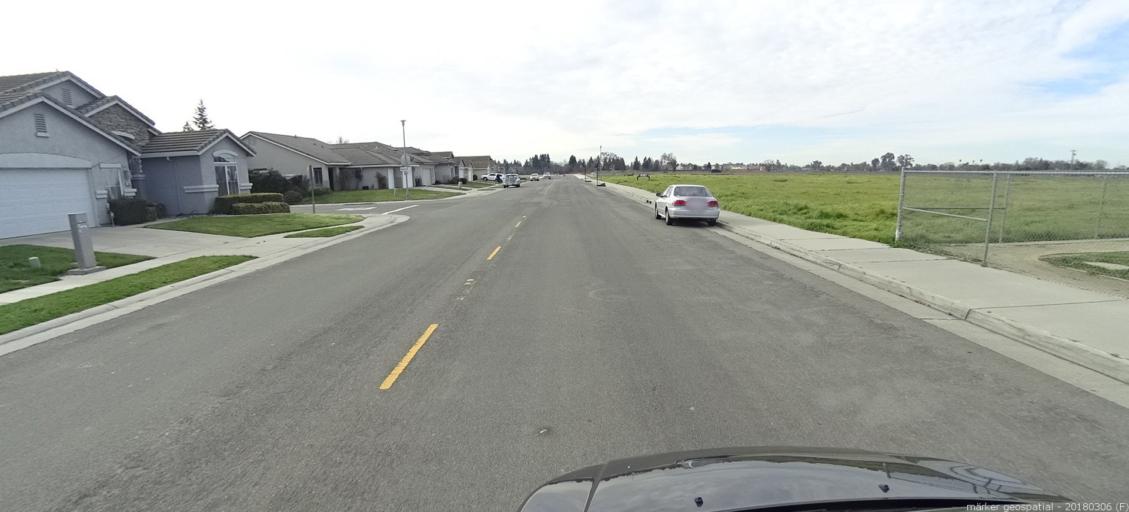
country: US
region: California
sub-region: Sacramento County
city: Vineyard
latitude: 38.4695
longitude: -121.3233
